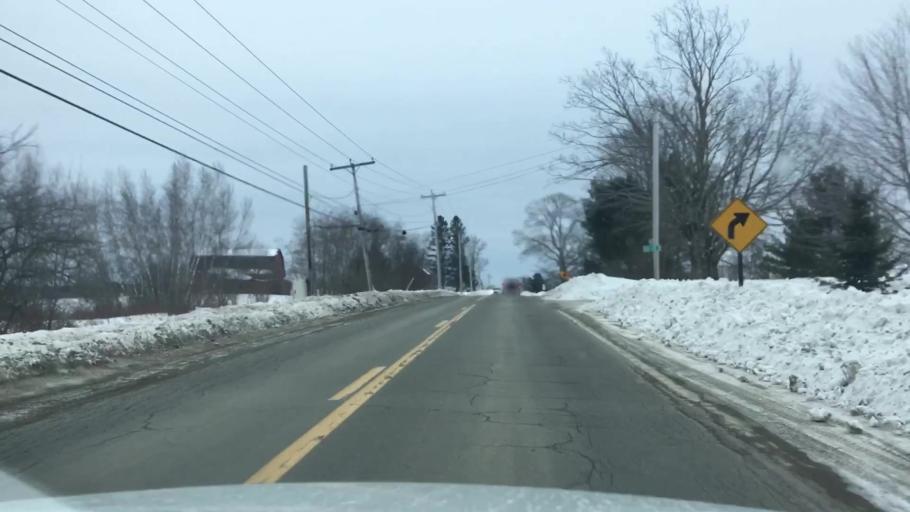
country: US
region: Maine
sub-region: Penobscot County
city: Charleston
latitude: 45.0315
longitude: -69.0316
